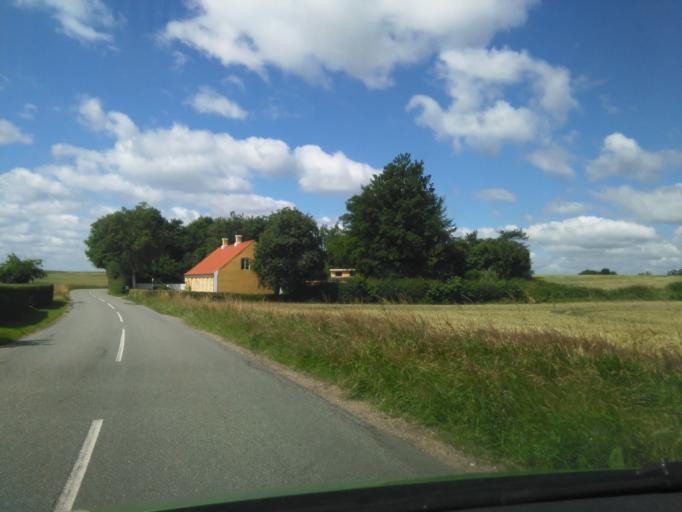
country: DK
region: Central Jutland
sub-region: Syddjurs Kommune
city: Ronde
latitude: 56.1971
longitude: 10.4318
